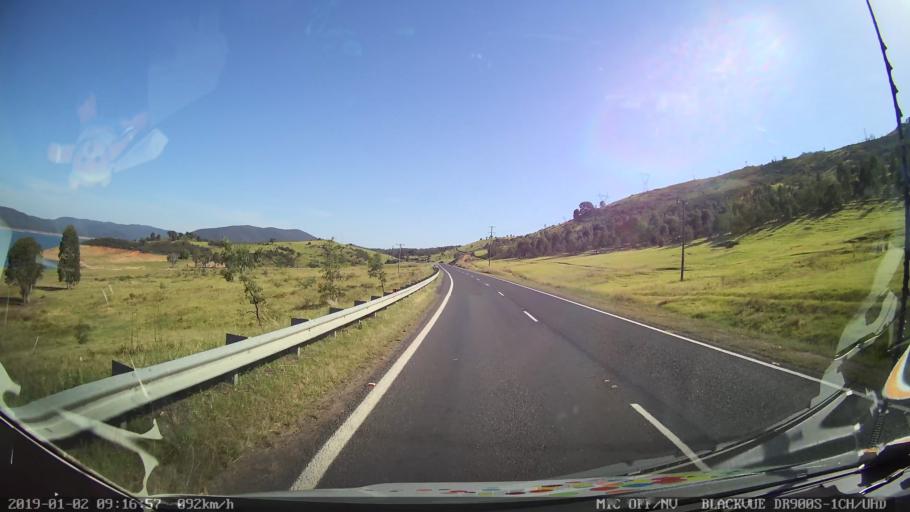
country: AU
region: New South Wales
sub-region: Tumut Shire
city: Tumut
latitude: -35.4474
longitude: 148.2859
